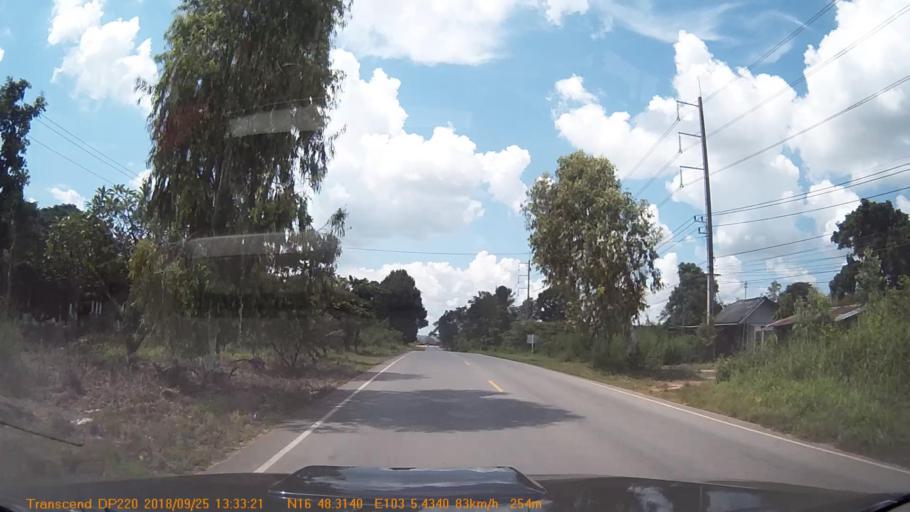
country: TH
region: Khon Kaen
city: Kranuan
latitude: 16.8053
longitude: 103.0905
